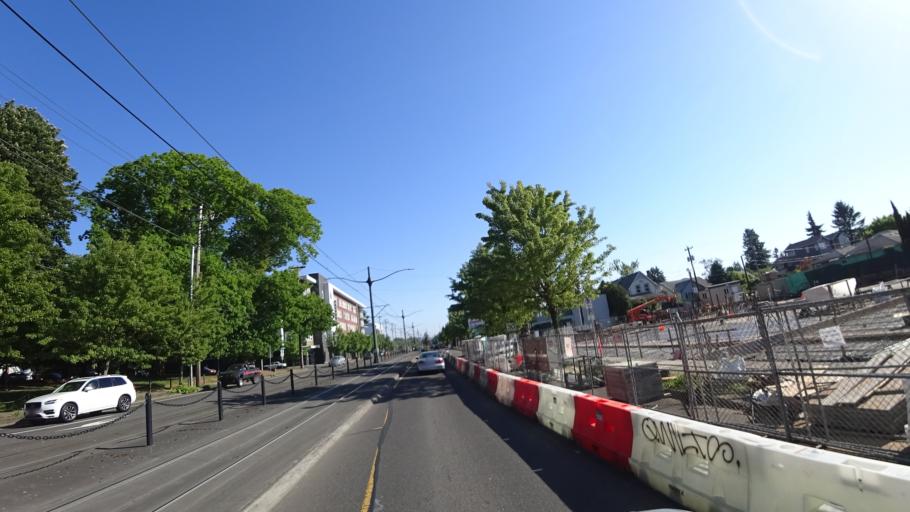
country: US
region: Oregon
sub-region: Multnomah County
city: Portland
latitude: 45.5617
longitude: -122.6823
